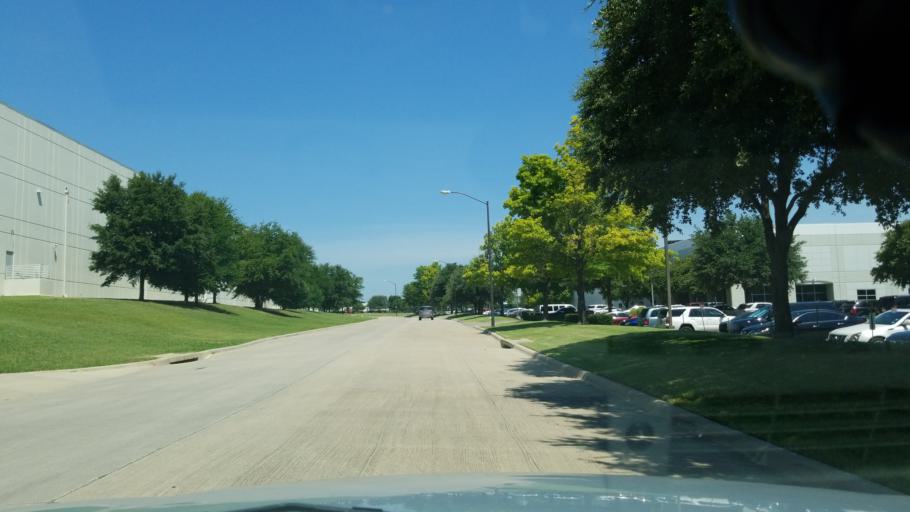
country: US
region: Texas
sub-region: Tarrant County
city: Euless
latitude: 32.8327
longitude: -97.0393
